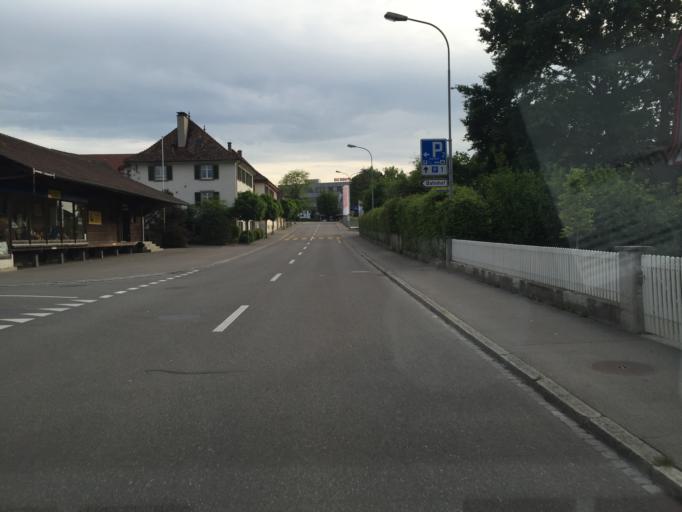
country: CH
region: Thurgau
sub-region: Frauenfeld District
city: Steckborn
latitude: 47.6640
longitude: 8.9786
